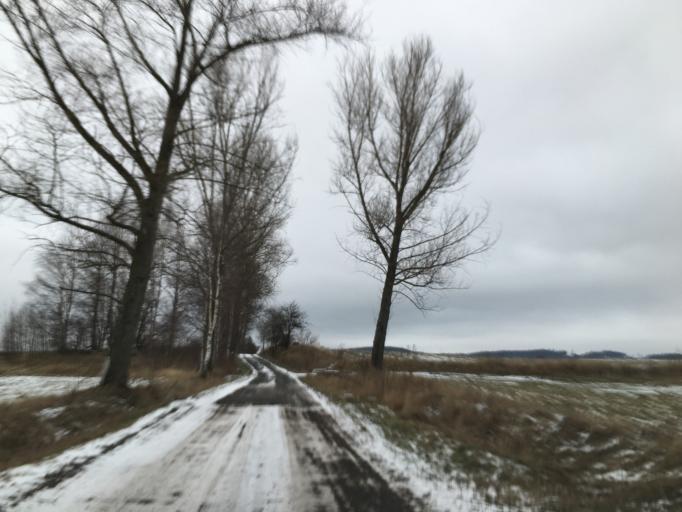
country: PL
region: Lower Silesian Voivodeship
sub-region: Powiat kamiennogorski
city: Krzeszow
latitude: 50.7013
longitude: 16.1044
